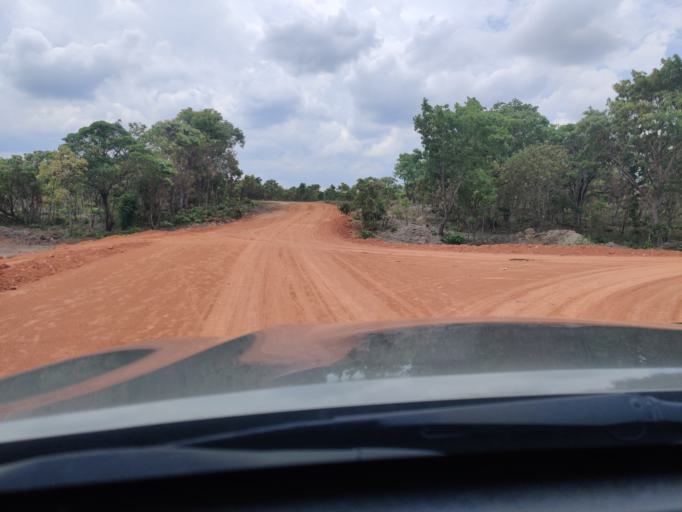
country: ZM
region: Central
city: Mkushi
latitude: -13.8504
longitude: 29.8878
